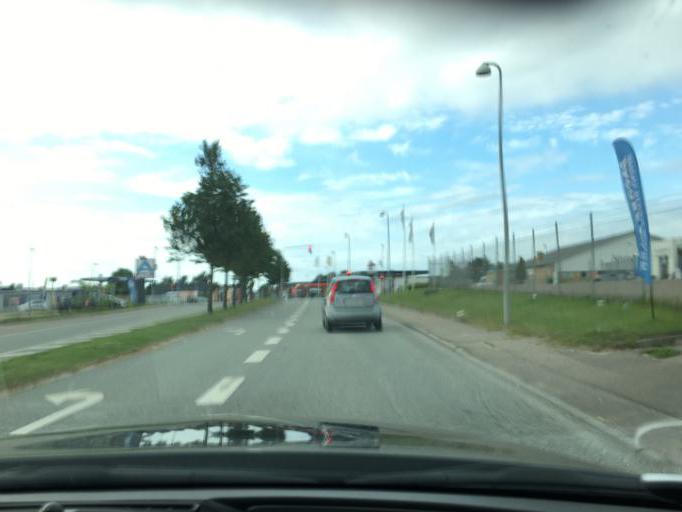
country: DK
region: Capital Region
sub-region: Gribskov Kommune
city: Helsinge
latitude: 56.0151
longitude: 12.1995
